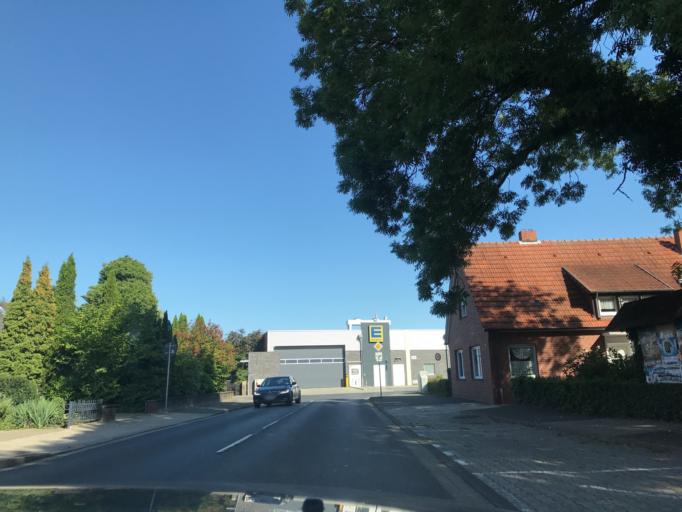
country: DE
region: Lower Saxony
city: Haselunne
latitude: 52.6730
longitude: 7.4828
